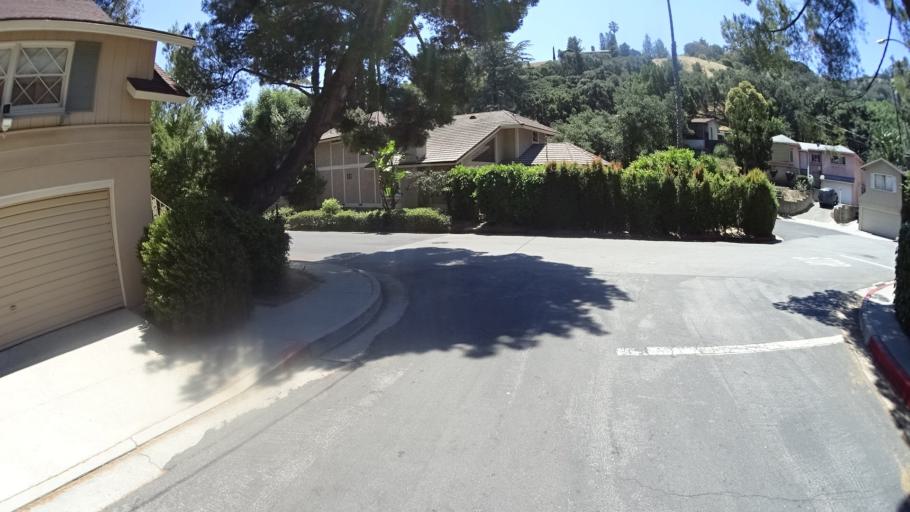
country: US
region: California
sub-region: Los Angeles County
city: Universal City
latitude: 34.1331
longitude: -118.3646
